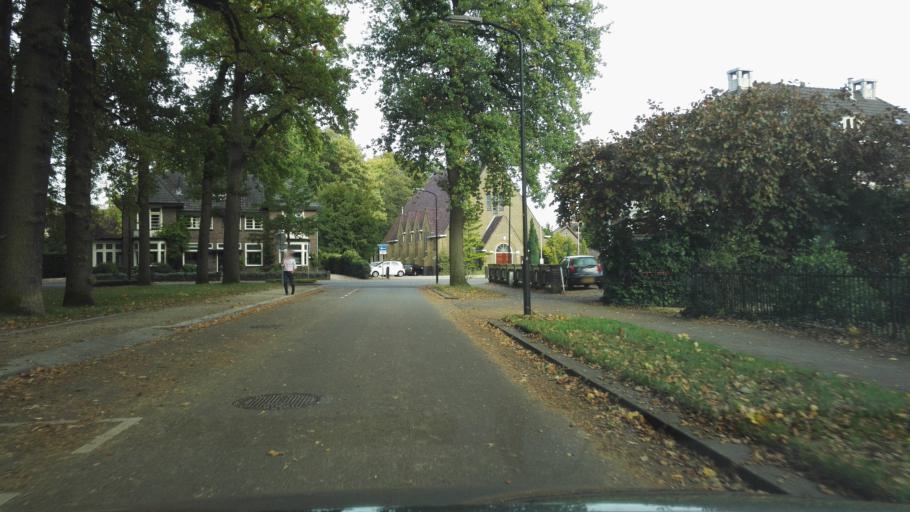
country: NL
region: Gelderland
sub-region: Gemeente Apeldoorn
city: Apeldoorn
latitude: 52.2181
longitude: 5.9624
